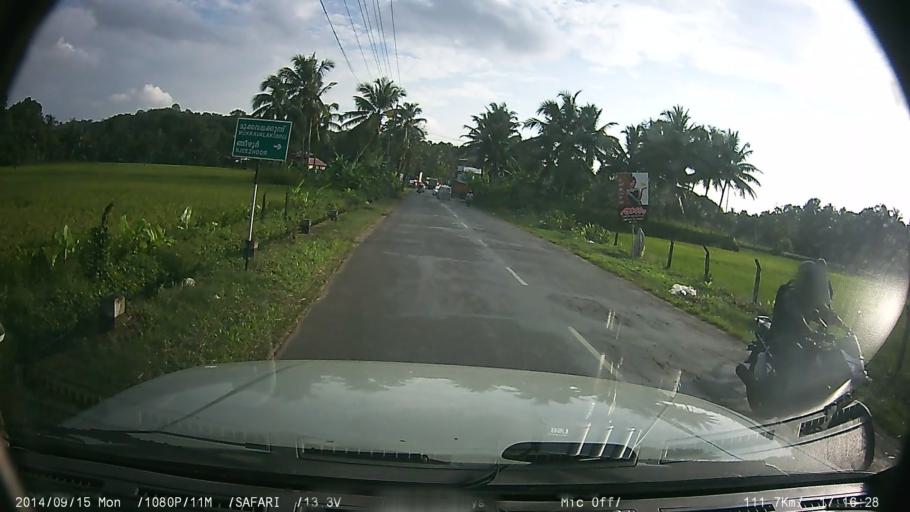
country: IN
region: Kerala
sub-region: Kottayam
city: Palackattumala
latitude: 9.7644
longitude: 76.5675
